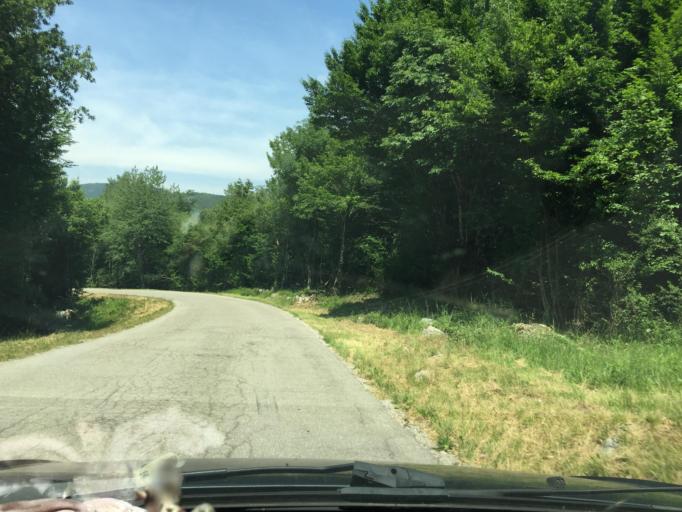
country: HR
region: Istarska
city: Buzet
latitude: 45.4607
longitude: 14.1358
